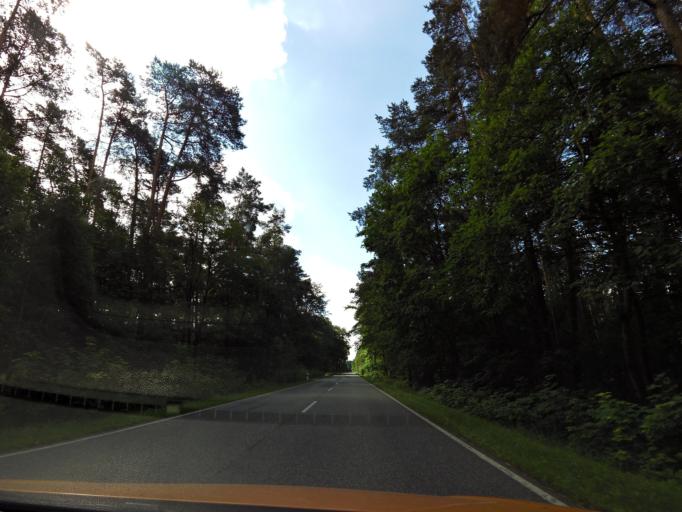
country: DE
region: Mecklenburg-Vorpommern
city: Krakow am See
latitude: 53.5700
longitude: 12.2719
